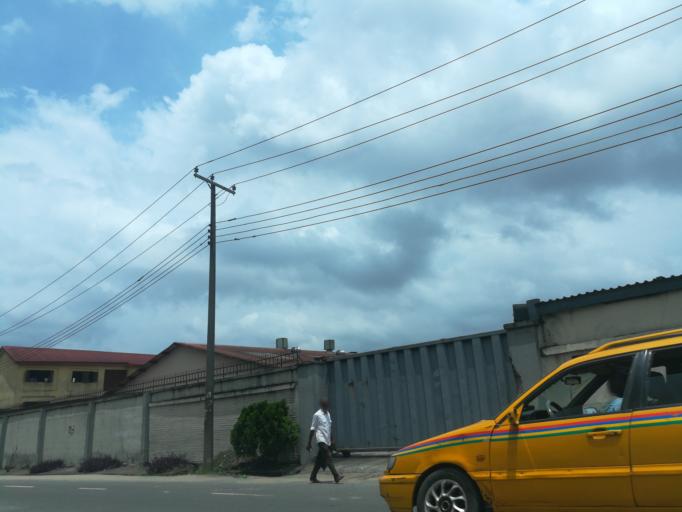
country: NG
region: Lagos
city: Oshodi
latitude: 6.5560
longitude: 3.3557
